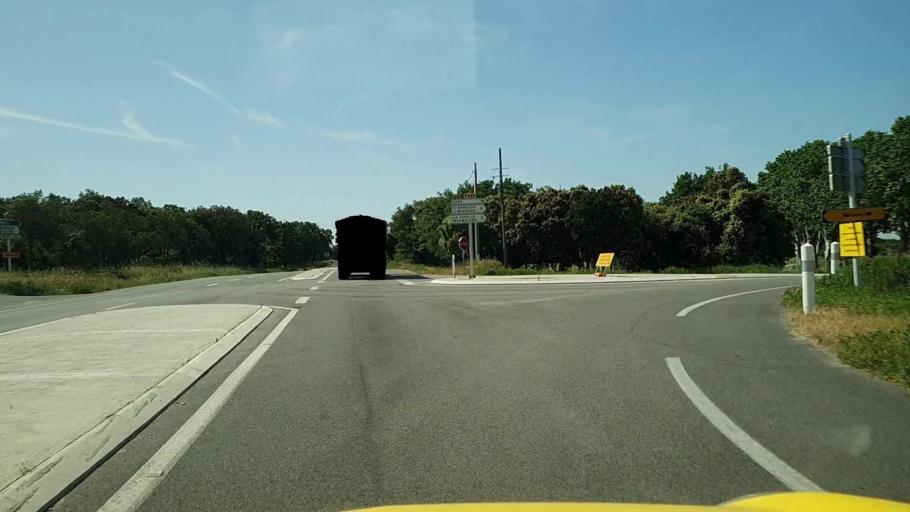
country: FR
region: Languedoc-Roussillon
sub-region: Departement du Gard
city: Connaux
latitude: 44.0566
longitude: 4.5706
